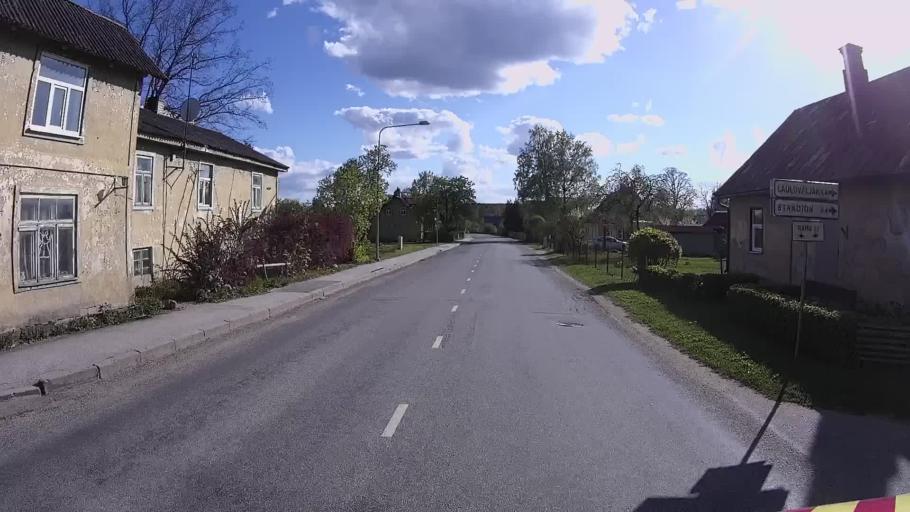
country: EE
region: Jogevamaa
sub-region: Poltsamaa linn
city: Poltsamaa
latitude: 58.6580
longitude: 25.9848
